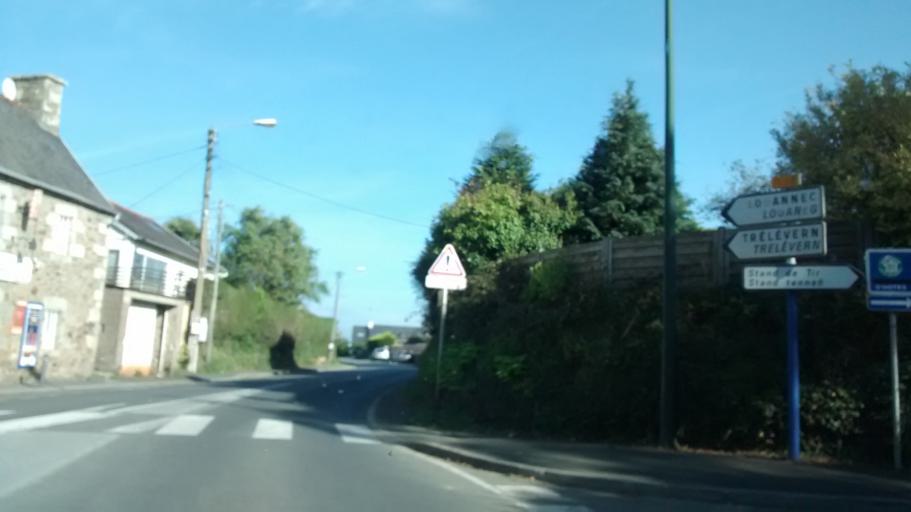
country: FR
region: Brittany
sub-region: Departement des Cotes-d'Armor
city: Lannion
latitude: 48.7511
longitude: -3.4456
